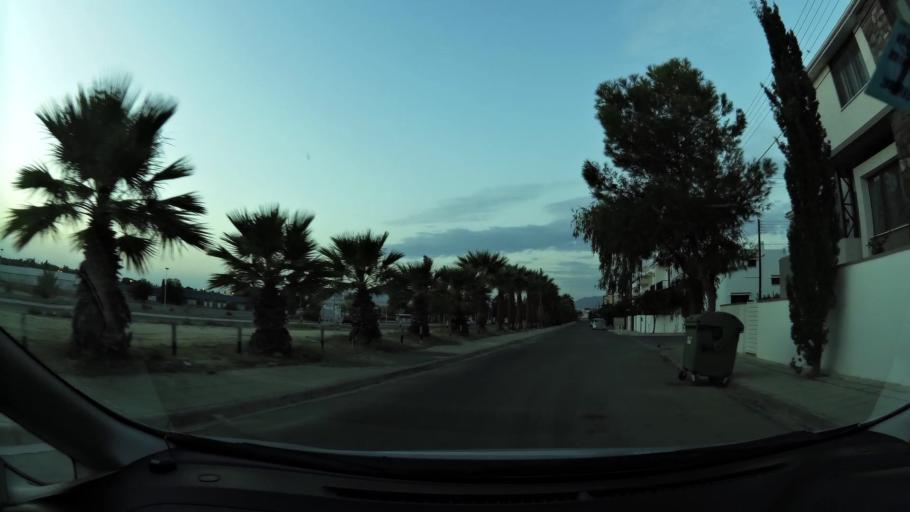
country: CY
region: Lefkosia
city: Nicosia
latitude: 35.1486
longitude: 33.3176
